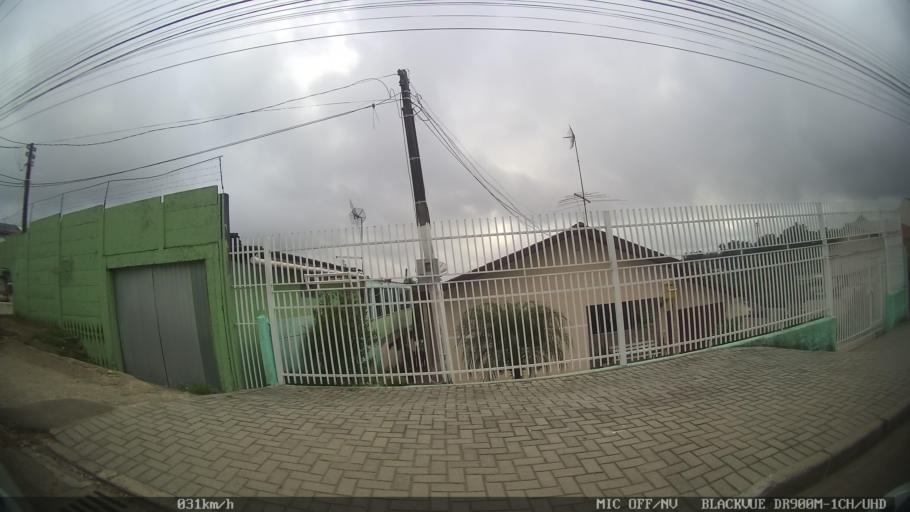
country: BR
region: Parana
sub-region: Almirante Tamandare
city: Almirante Tamandare
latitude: -25.3548
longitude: -49.2719
